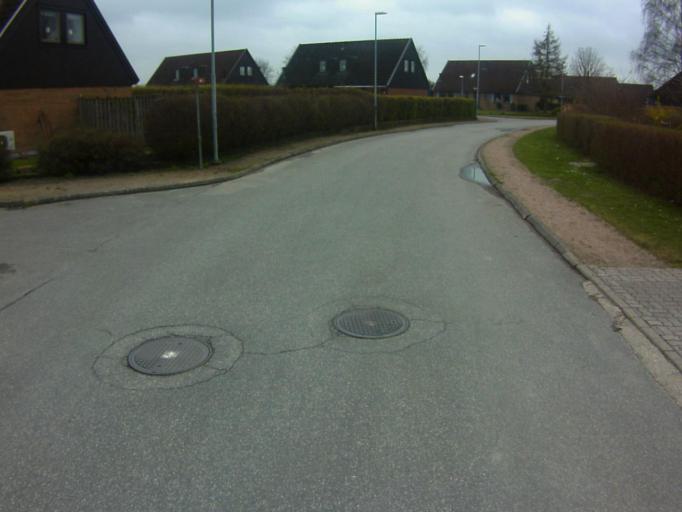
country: SE
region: Skane
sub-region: Kavlinge Kommun
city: Kaevlinge
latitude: 55.7735
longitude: 13.1020
